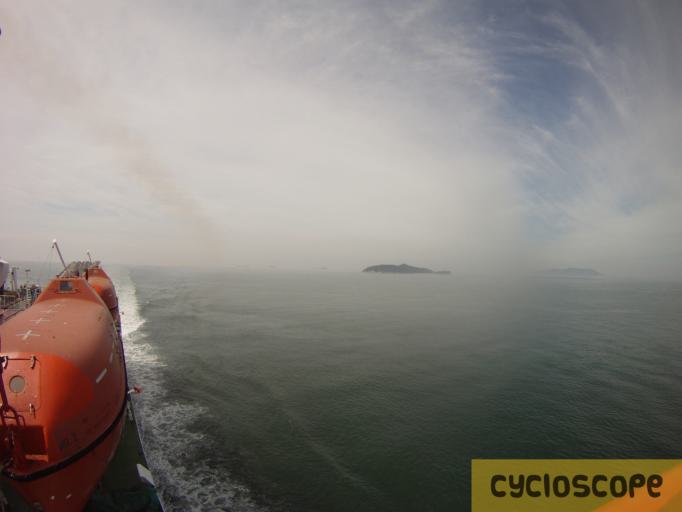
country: KR
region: Chungcheongnam-do
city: Taesal-li
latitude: 37.2802
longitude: 126.4253
